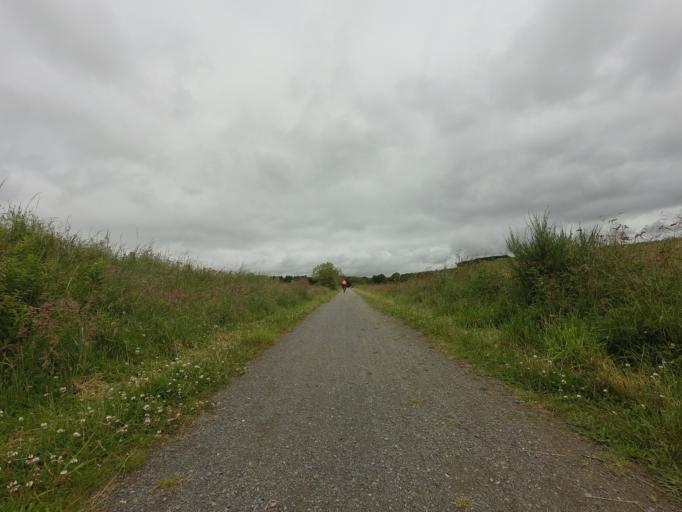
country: GB
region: Scotland
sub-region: Aberdeenshire
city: Mintlaw
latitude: 57.5155
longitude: -2.1352
